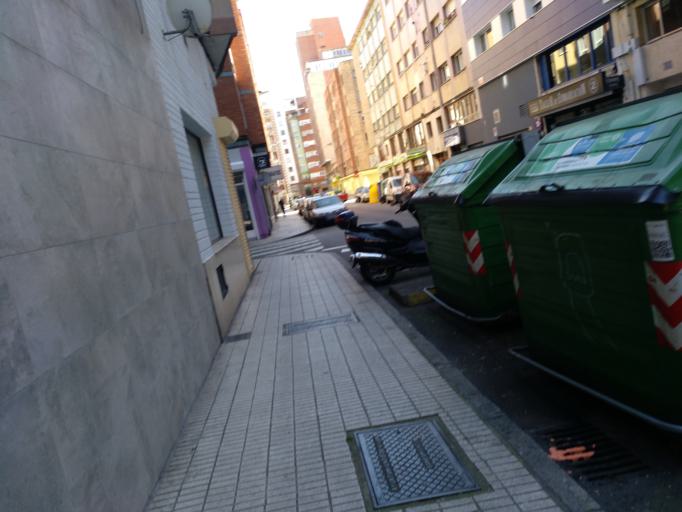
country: ES
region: Asturias
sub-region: Province of Asturias
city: Gijon
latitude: 43.5372
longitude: -5.6682
